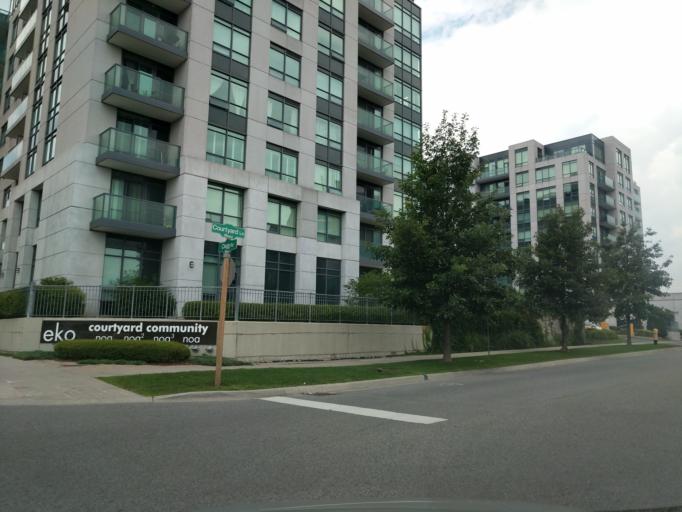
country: CA
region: Ontario
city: Markham
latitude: 43.8529
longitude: -79.3362
